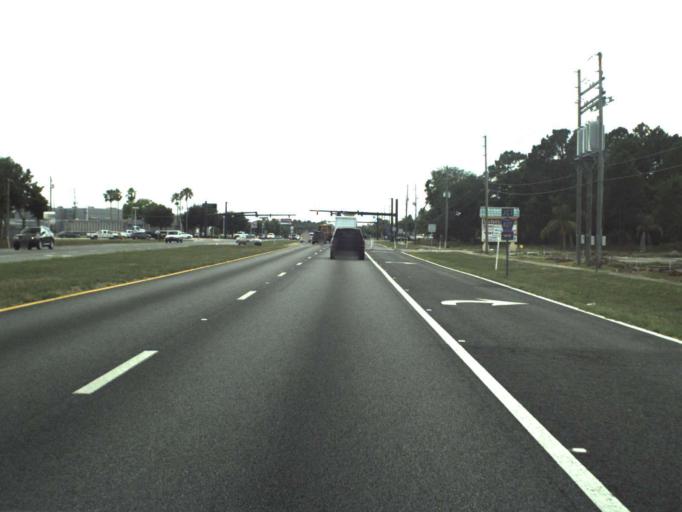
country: US
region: Florida
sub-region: Seminole County
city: Lake Mary
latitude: 28.7348
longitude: -81.3060
